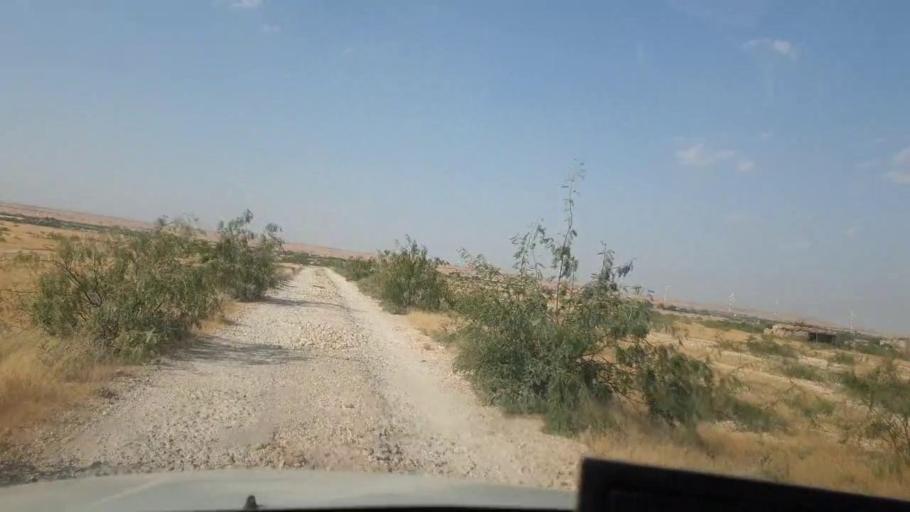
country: PK
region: Sindh
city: Daro Mehar
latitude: 25.0729
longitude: 68.0959
